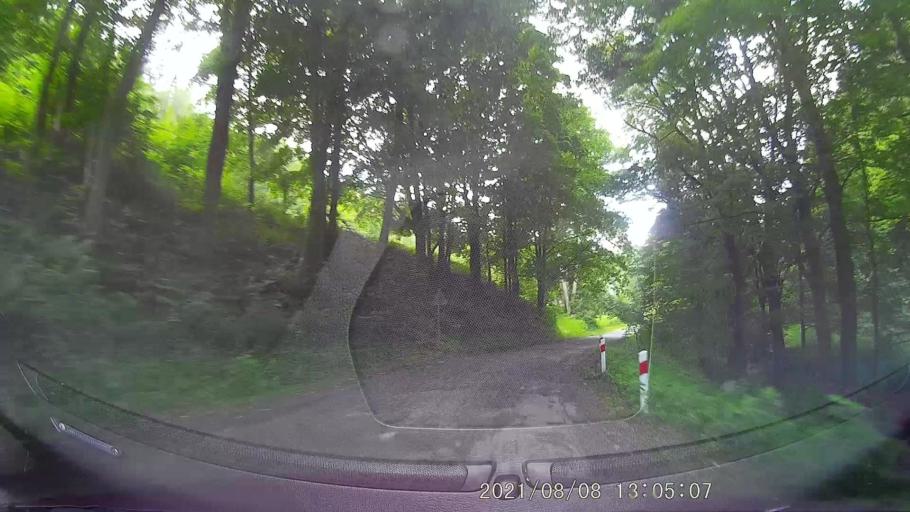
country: PL
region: Lower Silesian Voivodeship
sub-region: Powiat klodzki
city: Lewin Klodzki
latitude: 50.4287
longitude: 16.3068
